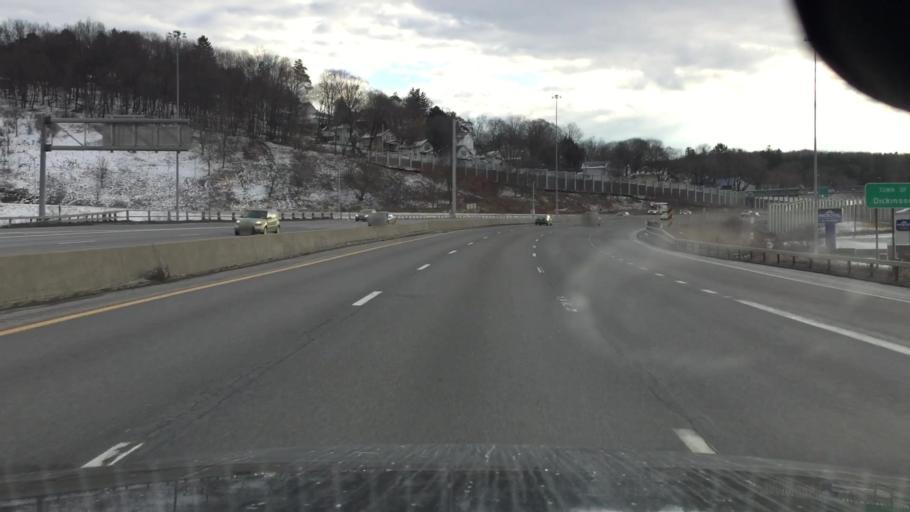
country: US
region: New York
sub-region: Broome County
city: Johnson City
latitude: 42.1199
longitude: -75.9469
